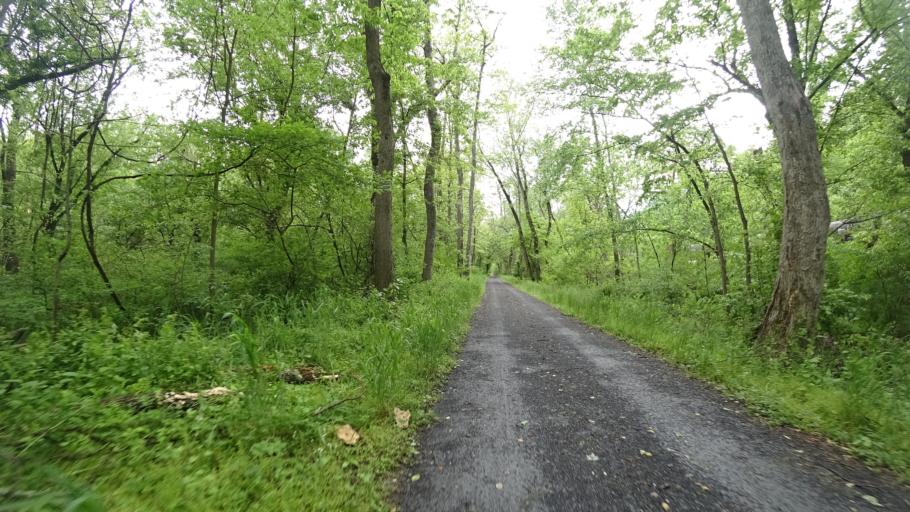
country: US
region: Maryland
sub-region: Frederick County
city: Brunswick
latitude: 39.3082
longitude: -77.5831
